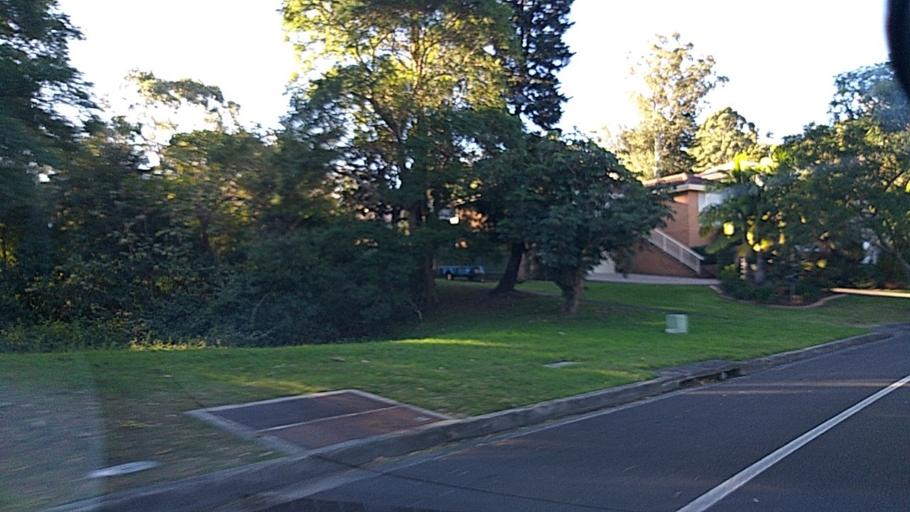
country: AU
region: New South Wales
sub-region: Wollongong
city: Cordeaux Heights
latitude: -34.4333
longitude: 150.8464
